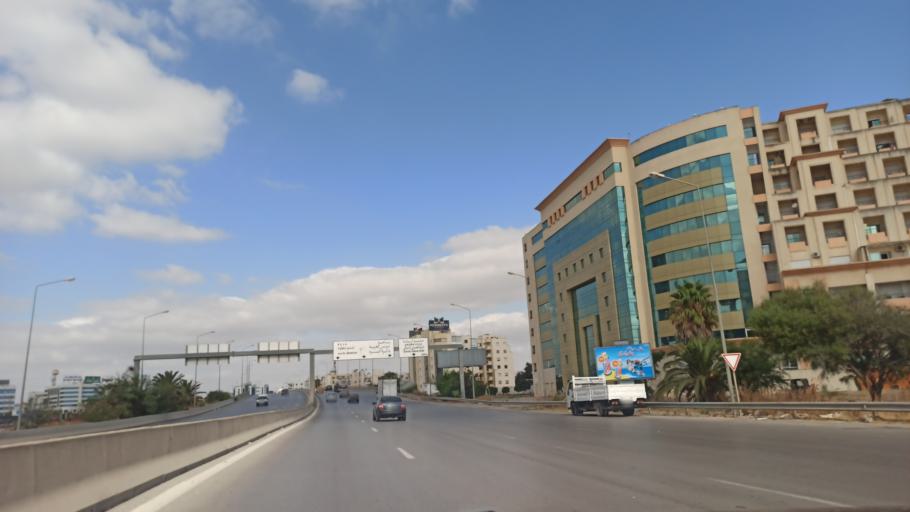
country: TN
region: Ariana
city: Ariana
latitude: 36.8511
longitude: 10.1991
